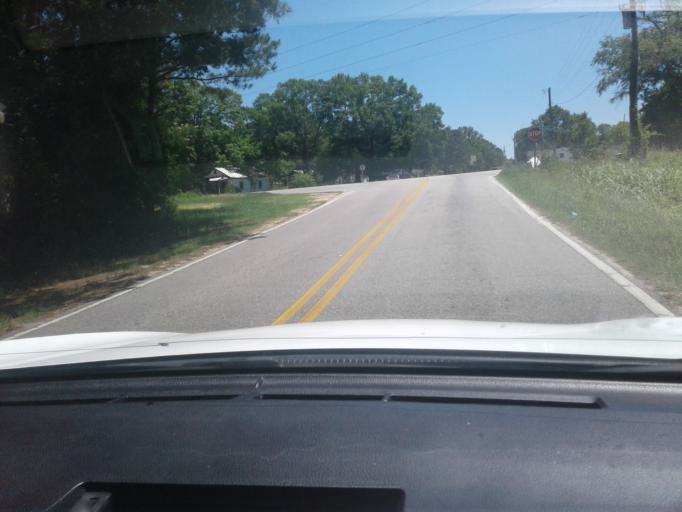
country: US
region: North Carolina
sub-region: Harnett County
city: Erwin
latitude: 35.3187
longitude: -78.7219
